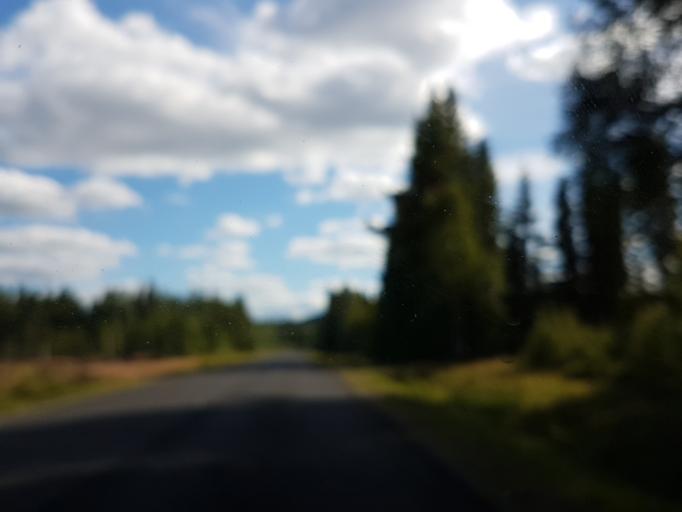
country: SE
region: Vaesterbotten
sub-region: Skelleftea Kommun
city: Burtraesk
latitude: 64.3008
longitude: 20.5275
